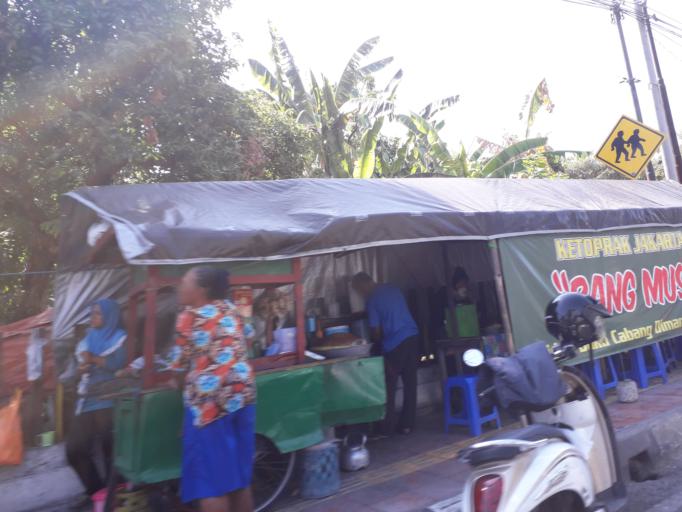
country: ID
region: Daerah Istimewa Yogyakarta
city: Yogyakarta
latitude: -7.7781
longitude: 110.3758
